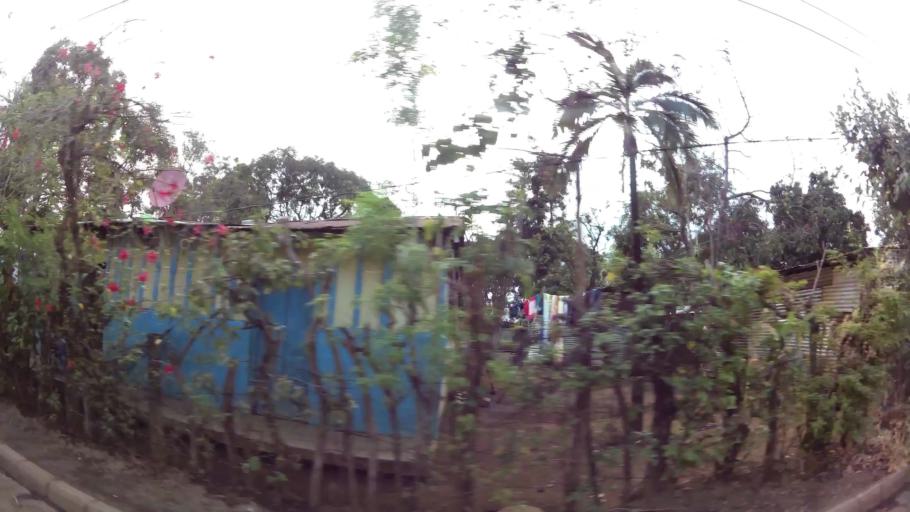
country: NI
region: Masaya
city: Masaya
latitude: 11.9838
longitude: -86.1050
